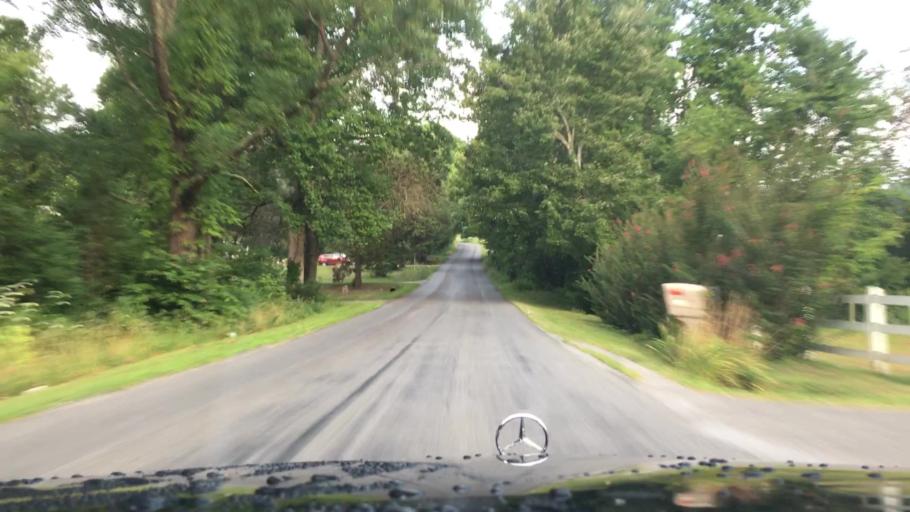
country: US
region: Virginia
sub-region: Campbell County
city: Altavista
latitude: 37.1460
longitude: -79.2842
